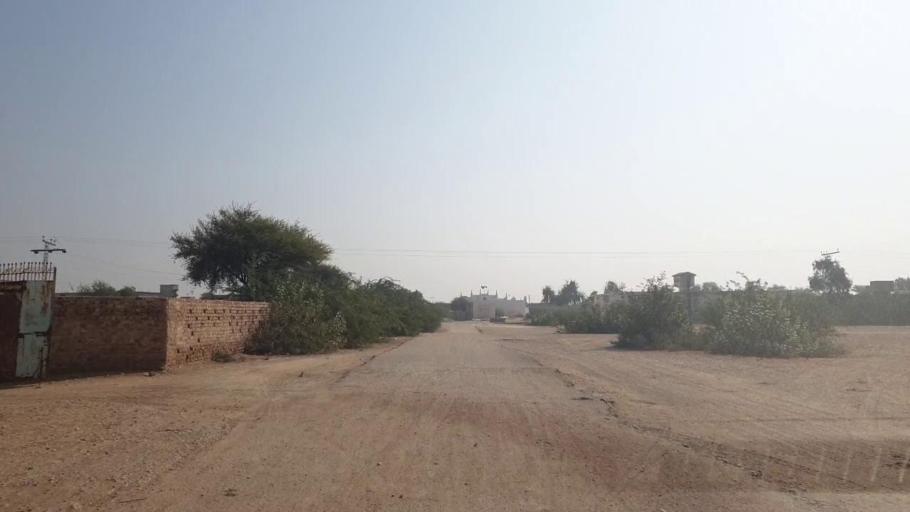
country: PK
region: Sindh
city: Jamshoro
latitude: 25.5335
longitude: 68.3406
